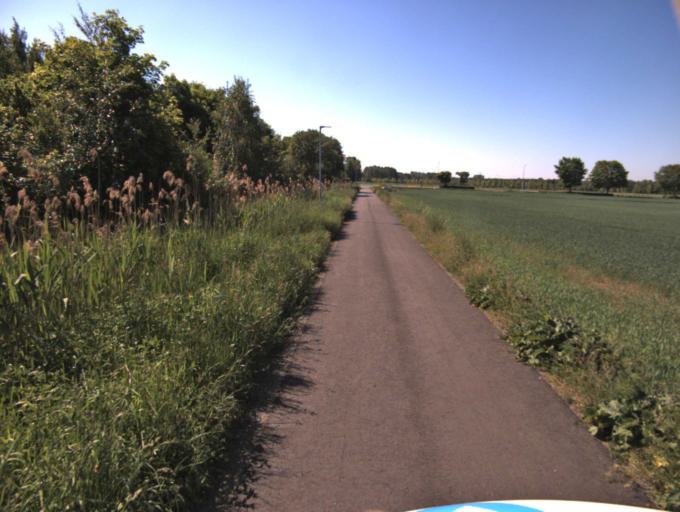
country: SE
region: Skane
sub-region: Kristianstads Kommun
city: Kristianstad
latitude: 56.0308
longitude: 14.1908
